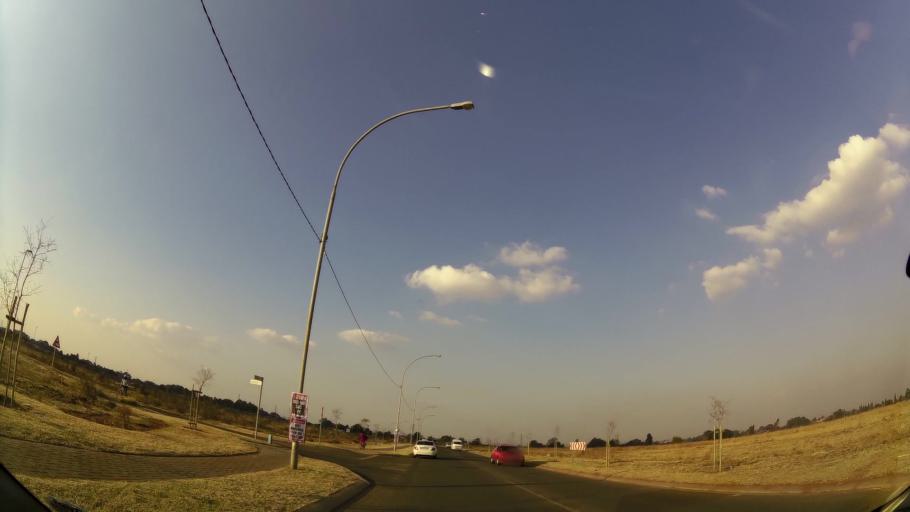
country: ZA
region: Gauteng
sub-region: Ekurhuleni Metropolitan Municipality
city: Benoni
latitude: -26.1323
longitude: 28.3793
